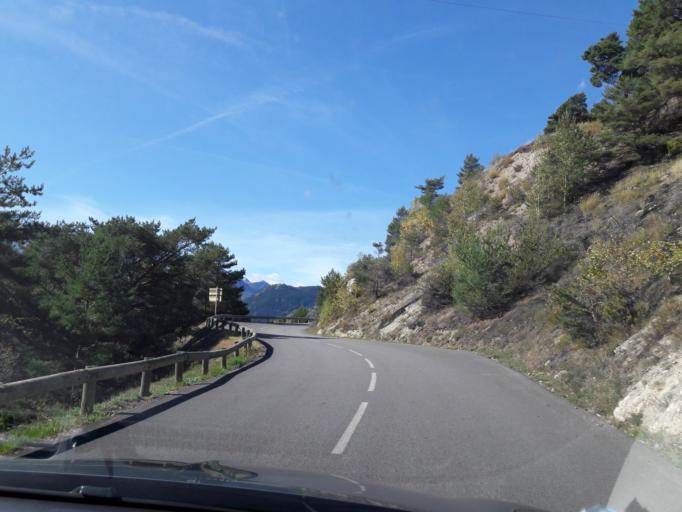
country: FR
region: Rhone-Alpes
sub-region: Departement de la Savoie
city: Modane
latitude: 45.2166
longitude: 6.7178
